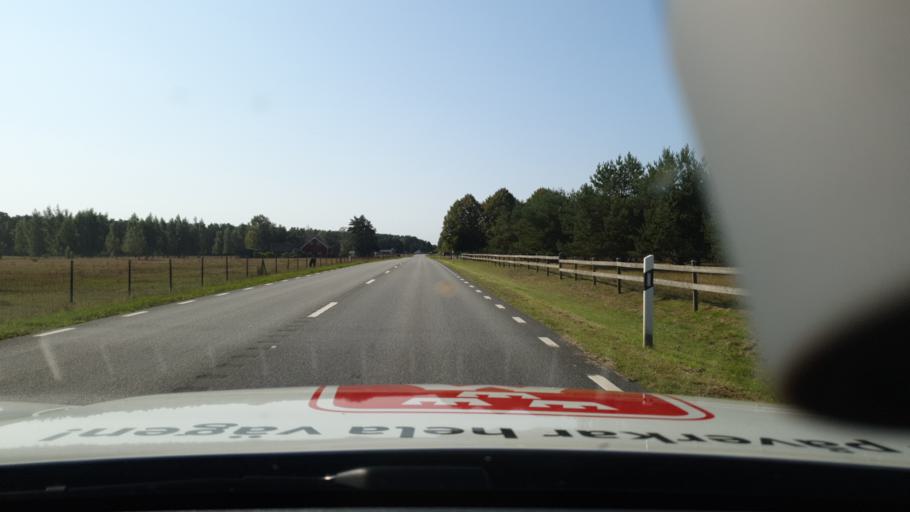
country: SE
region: Skane
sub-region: Kristianstads Kommun
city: Ahus
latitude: 55.8947
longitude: 14.2501
